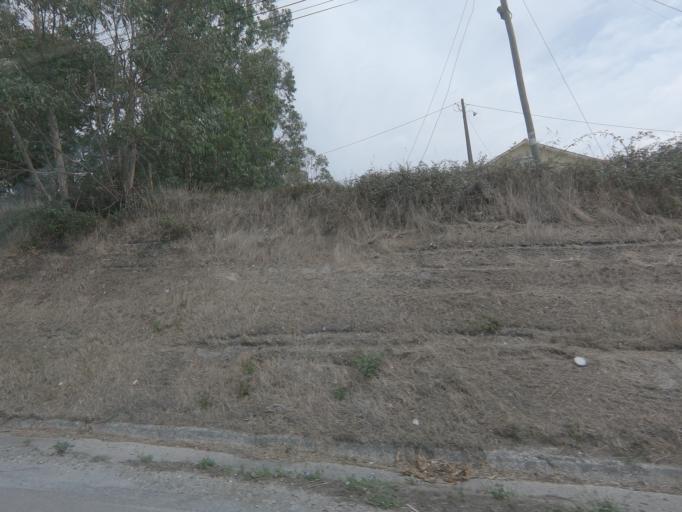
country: PT
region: Leiria
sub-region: Leiria
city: Caranguejeira
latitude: 39.8118
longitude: -8.7382
